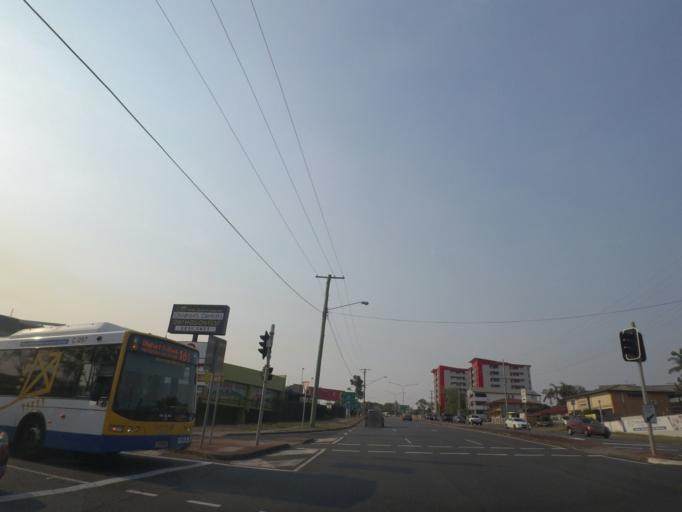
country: AU
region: Queensland
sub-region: Brisbane
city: Upper Mount Gravatt
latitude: -27.5663
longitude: 153.0877
